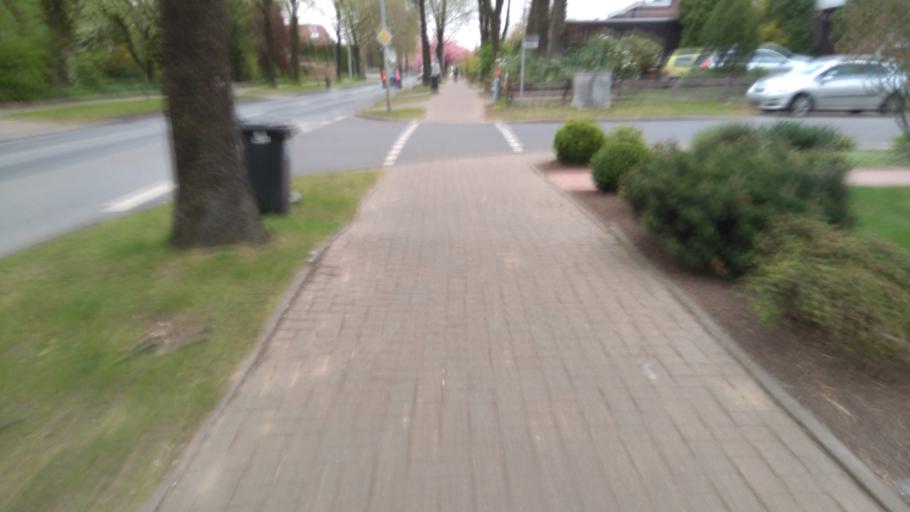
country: DE
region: Lower Saxony
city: Apensen
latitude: 53.4384
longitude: 9.6238
